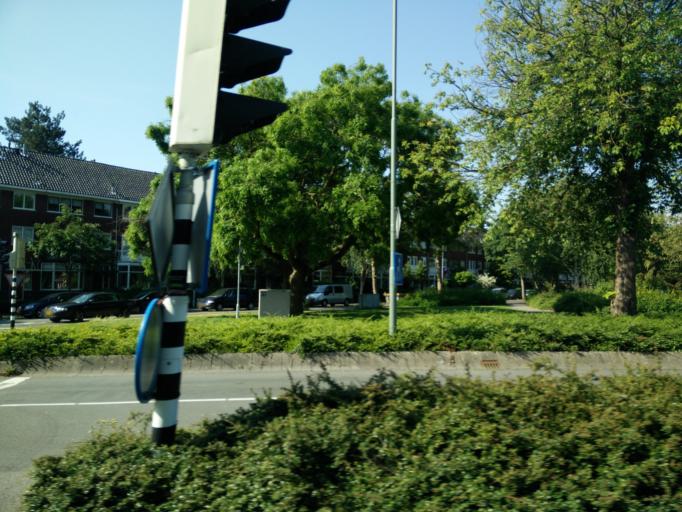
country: NL
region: South Holland
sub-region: Gemeente Dordrecht
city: Dordrecht
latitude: 51.8065
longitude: 4.6618
